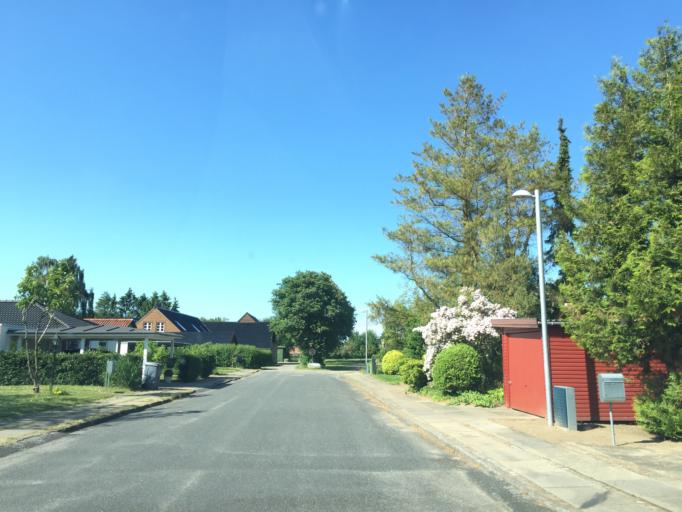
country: DK
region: South Denmark
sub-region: Odense Kommune
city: Odense
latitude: 55.3635
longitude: 10.4048
